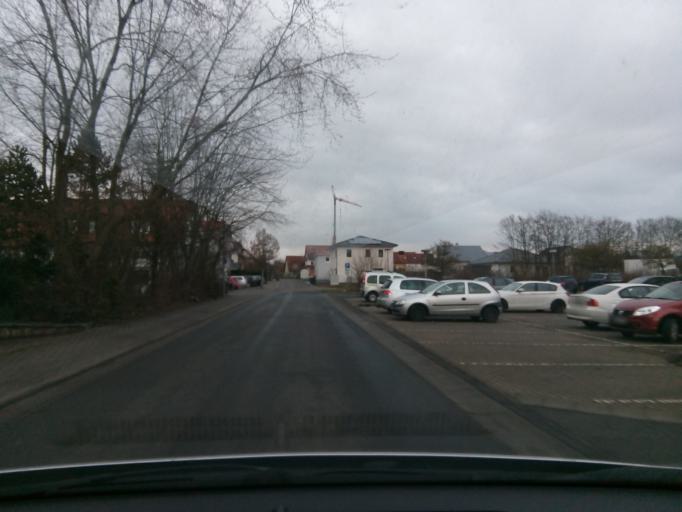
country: DE
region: Bavaria
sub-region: Regierungsbezirk Unterfranken
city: Gerolzhofen
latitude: 49.9015
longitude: 10.3556
